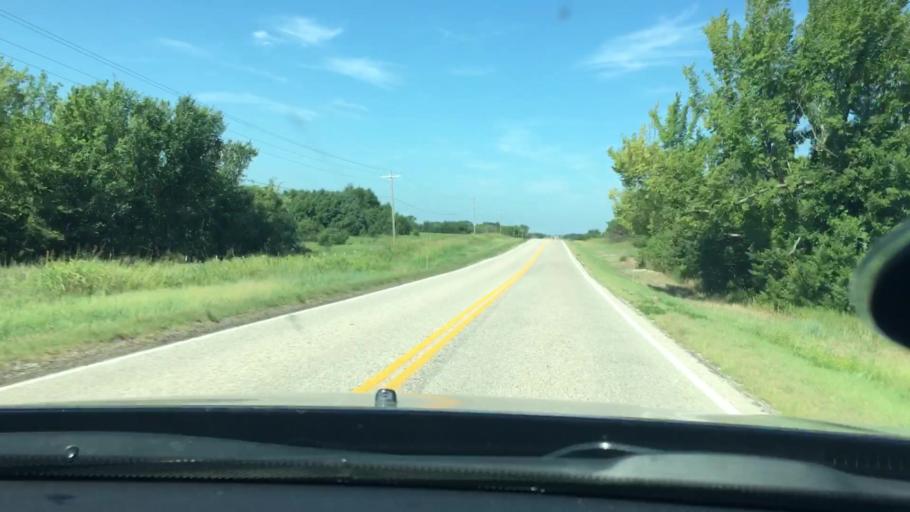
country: US
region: Oklahoma
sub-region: Johnston County
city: Tishomingo
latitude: 34.3614
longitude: -96.5610
